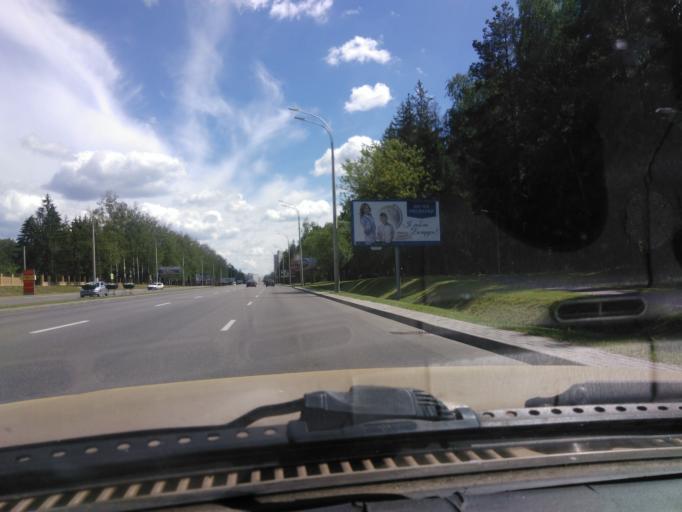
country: BY
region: Mogilev
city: Mahilyow
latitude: 53.9252
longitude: 30.2749
